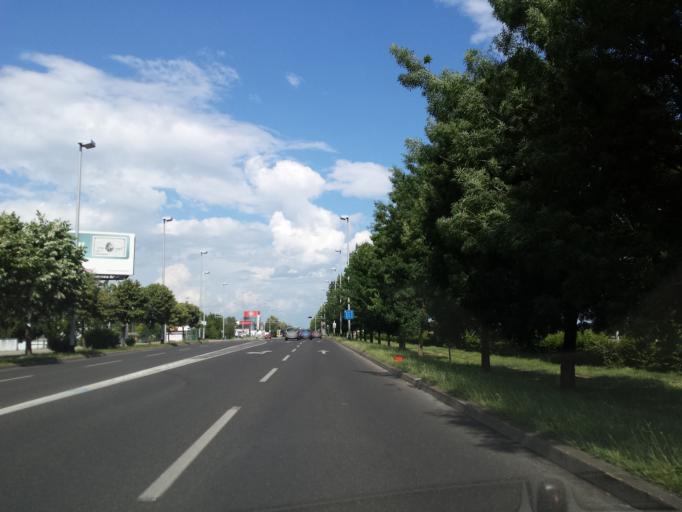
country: HR
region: Grad Zagreb
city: Dubrava
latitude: 45.8218
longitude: 16.0678
